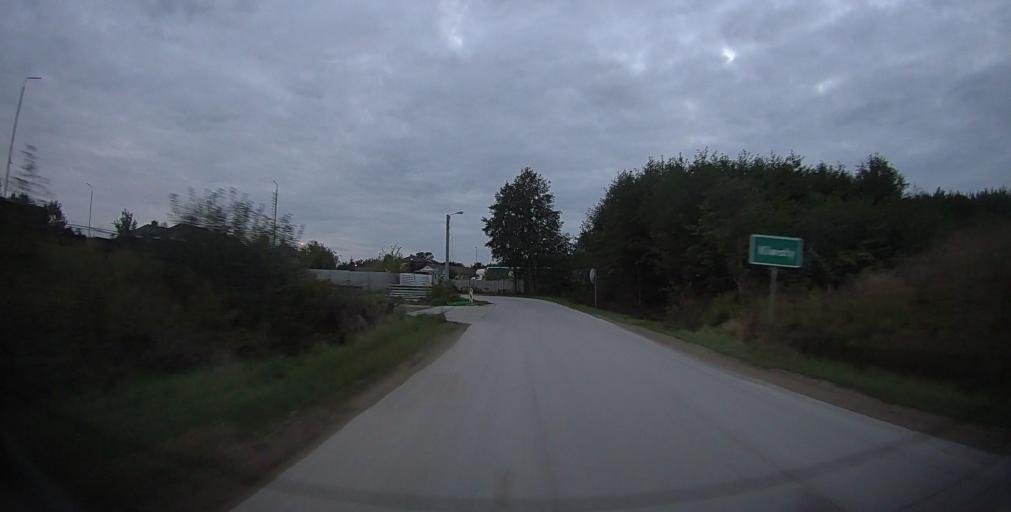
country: PL
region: Masovian Voivodeship
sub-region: Powiat radomski
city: Jedlinsk
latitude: 51.4601
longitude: 21.1214
